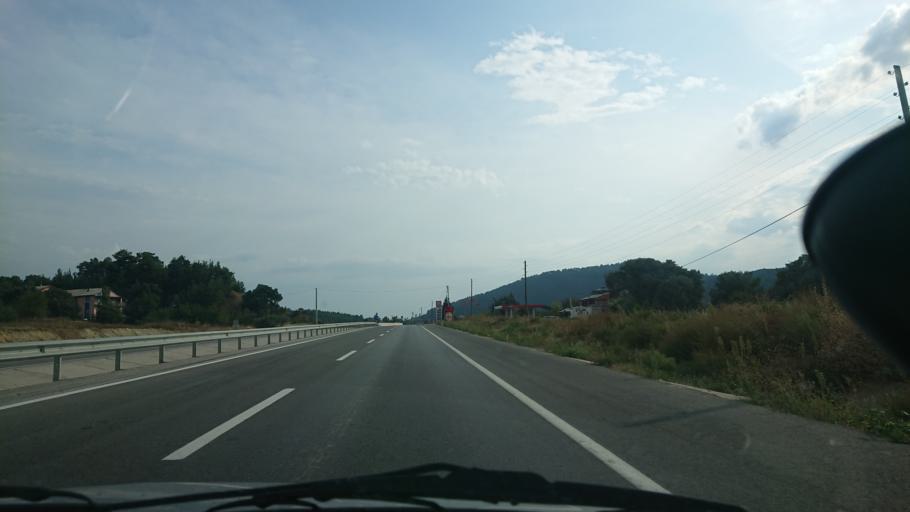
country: TR
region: Kuetahya
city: Gediz
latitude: 38.9222
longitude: 29.3033
